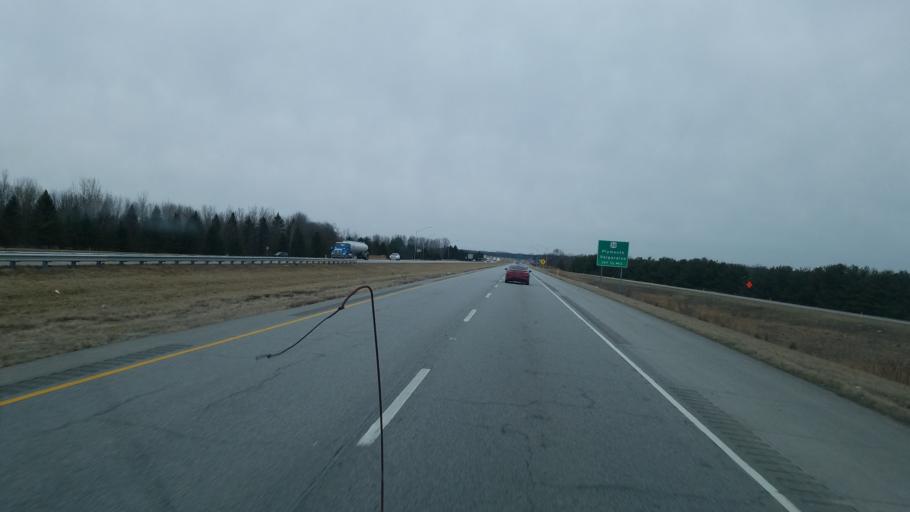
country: US
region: Indiana
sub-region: Porter County
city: Valparaiso
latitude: 41.4691
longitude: -87.0221
